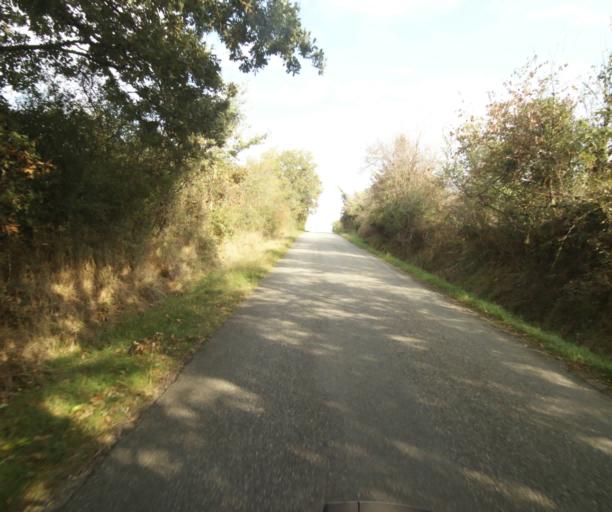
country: FR
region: Midi-Pyrenees
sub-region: Departement du Tarn-et-Garonne
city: Verdun-sur-Garonne
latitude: 43.8363
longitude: 1.1530
